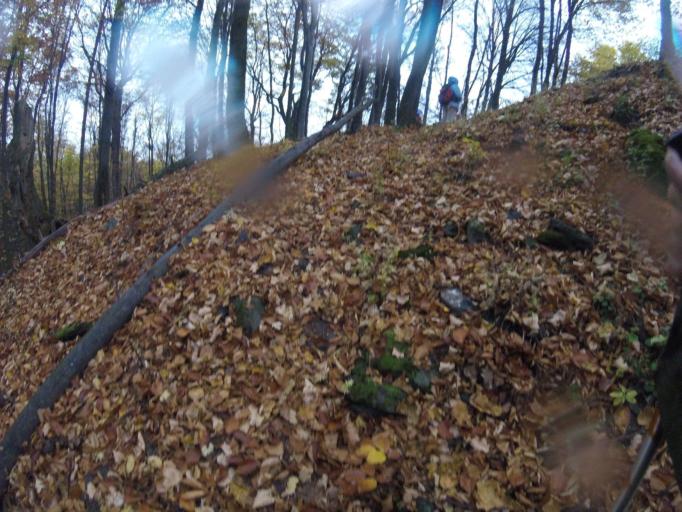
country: HU
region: Borsod-Abauj-Zemplen
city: Gonc
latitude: 48.4558
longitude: 21.3270
